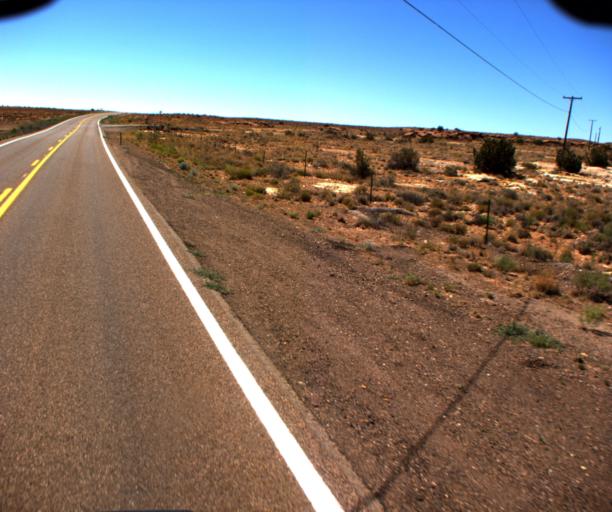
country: US
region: Arizona
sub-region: Navajo County
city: Winslow
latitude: 34.9750
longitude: -110.6524
